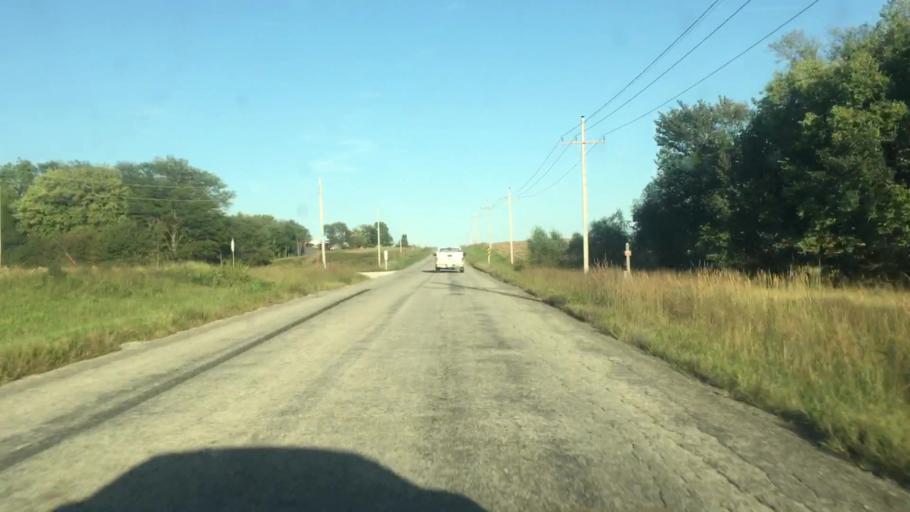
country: US
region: Kansas
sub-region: Brown County
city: Horton
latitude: 39.5656
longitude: -95.3778
